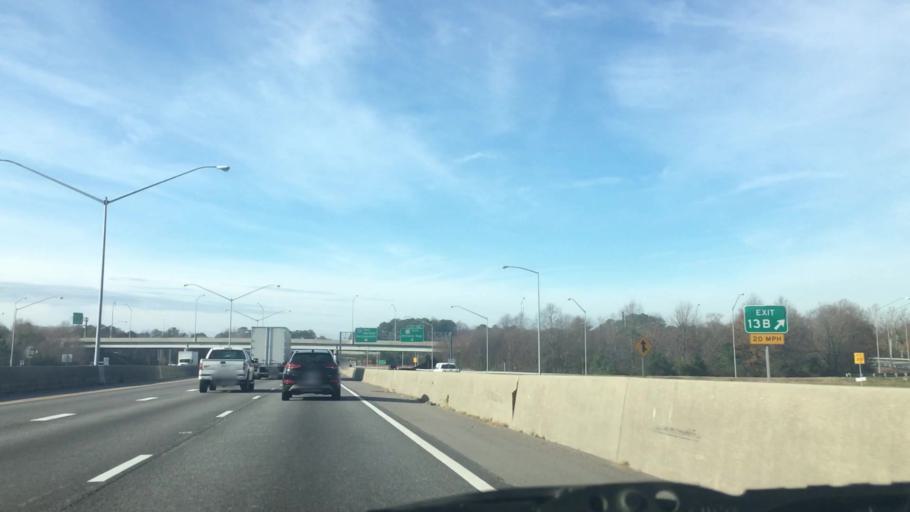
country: US
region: Virginia
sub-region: City of Chesapeake
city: Chesapeake
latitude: 36.8443
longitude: -76.2075
